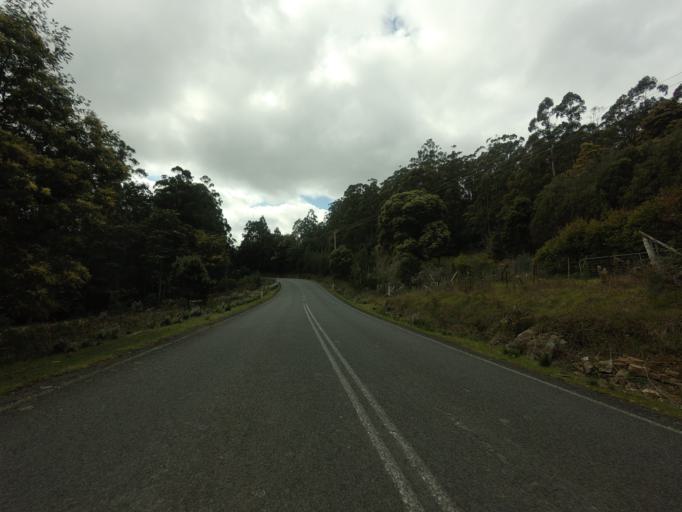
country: AU
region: Tasmania
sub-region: Huon Valley
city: Cygnet
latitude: -43.2774
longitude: 147.0089
